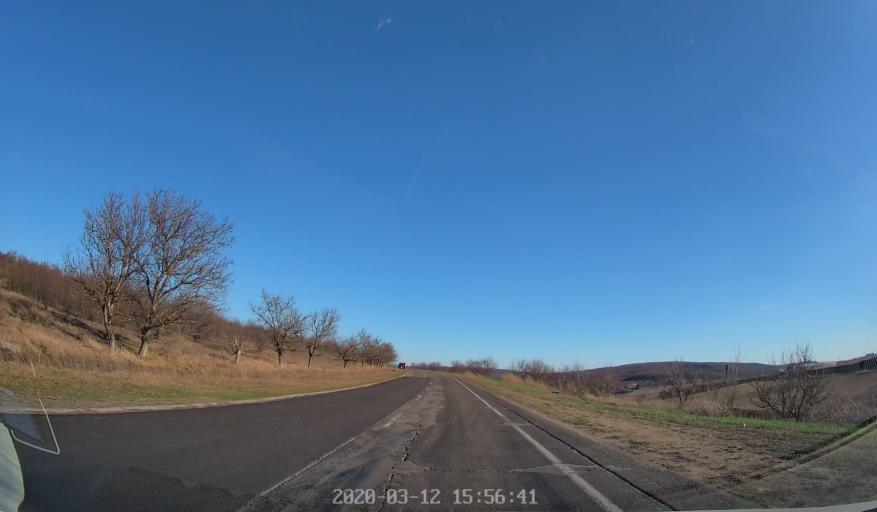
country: MD
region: Chisinau
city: Vadul lui Voda
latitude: 47.0602
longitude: 29.0356
